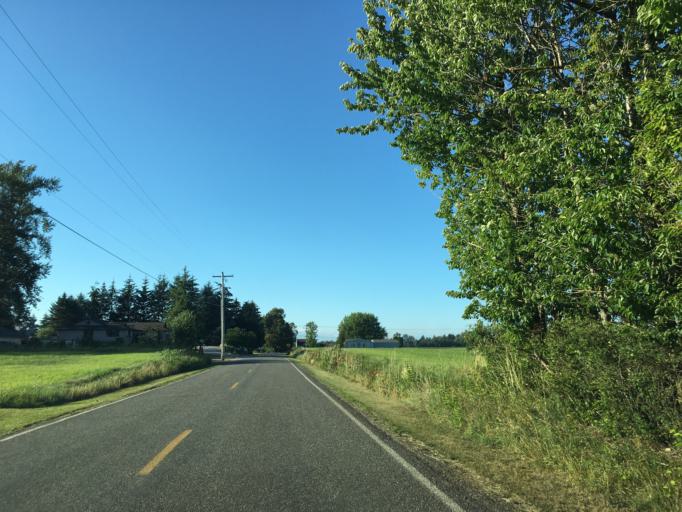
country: US
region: Washington
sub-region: Whatcom County
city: Everson
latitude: 48.9397
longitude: -122.3916
